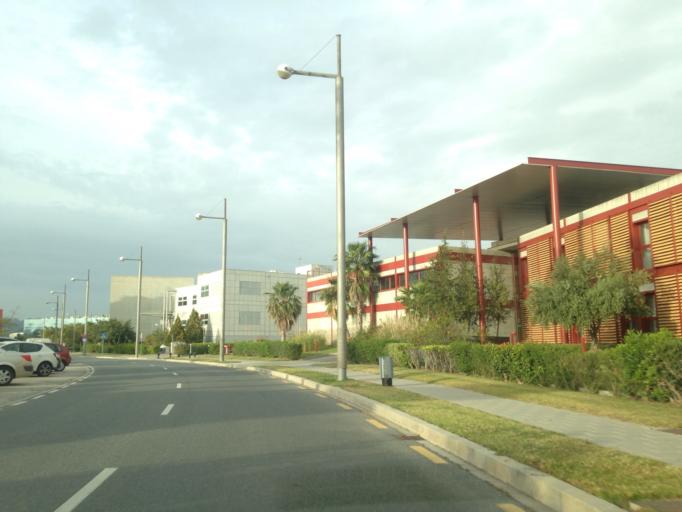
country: ES
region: Andalusia
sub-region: Provincia de Malaga
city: Estacion de Cartama
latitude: 36.7344
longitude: -4.5547
